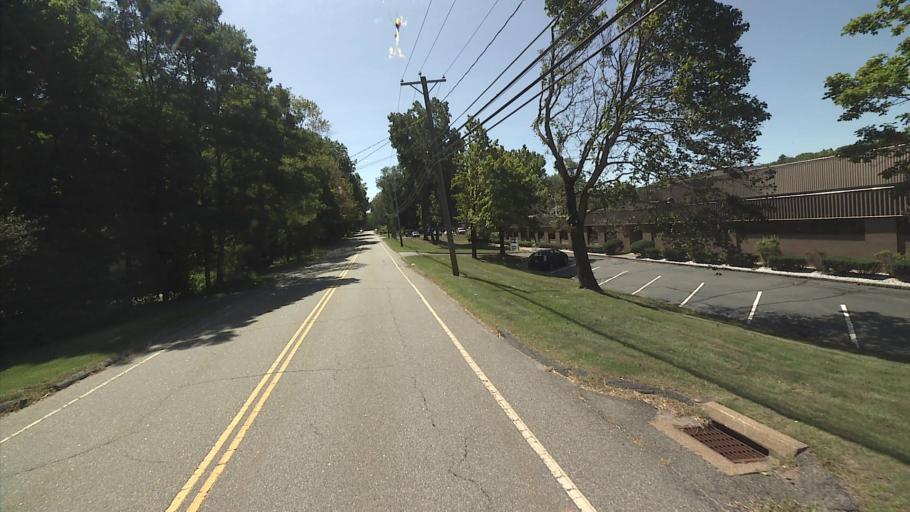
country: US
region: Connecticut
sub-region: Litchfield County
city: Litchfield
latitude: 41.7065
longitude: -73.2346
